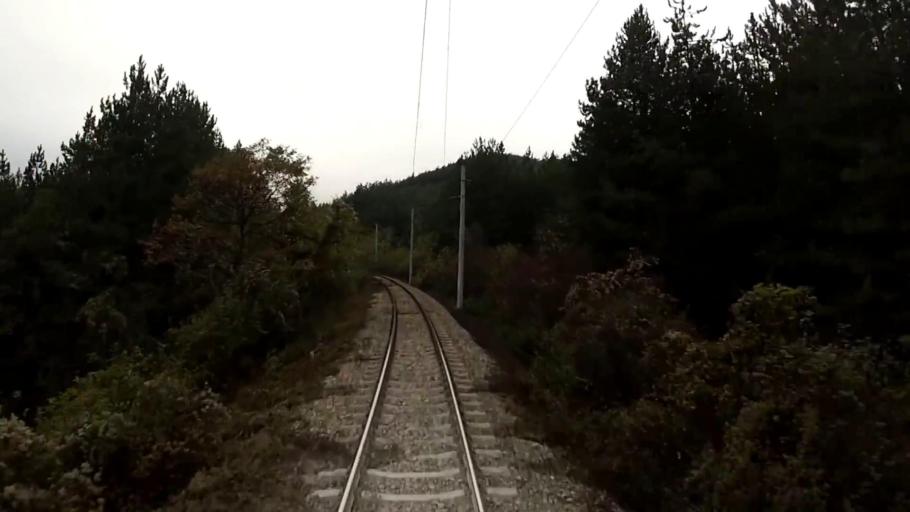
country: BG
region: Sofiya
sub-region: Obshtina Dragoman
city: Dragoman
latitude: 42.9469
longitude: 22.9012
